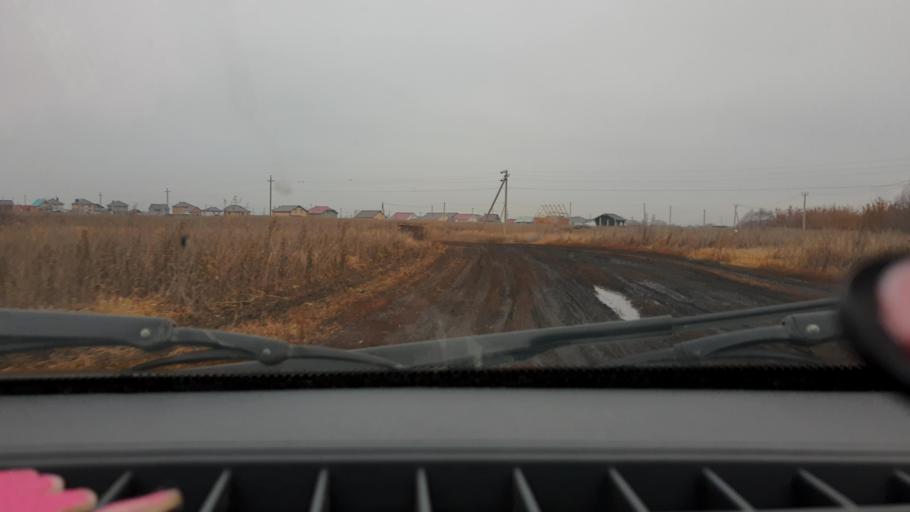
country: RU
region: Bashkortostan
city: Avdon
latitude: 54.5876
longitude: 55.8663
